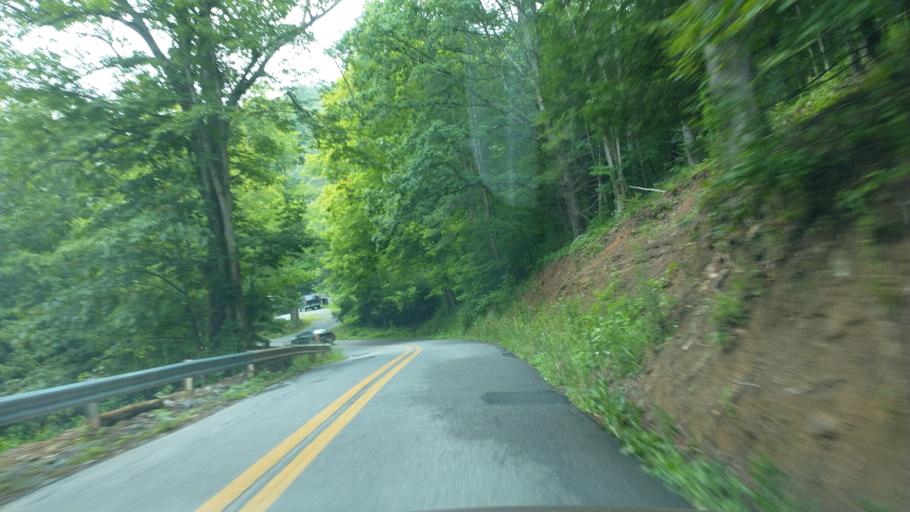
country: US
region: West Virginia
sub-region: Mercer County
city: Athens
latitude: 37.4281
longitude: -80.9920
